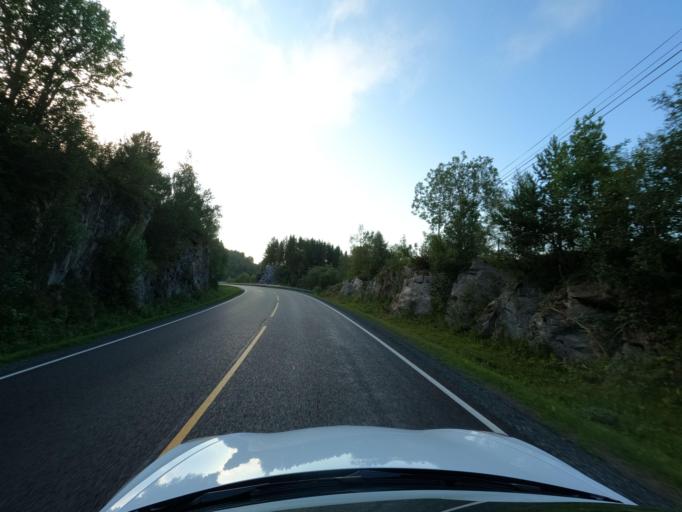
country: NO
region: Troms
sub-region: Skanland
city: Evenskjer
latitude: 68.6699
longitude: 16.5750
